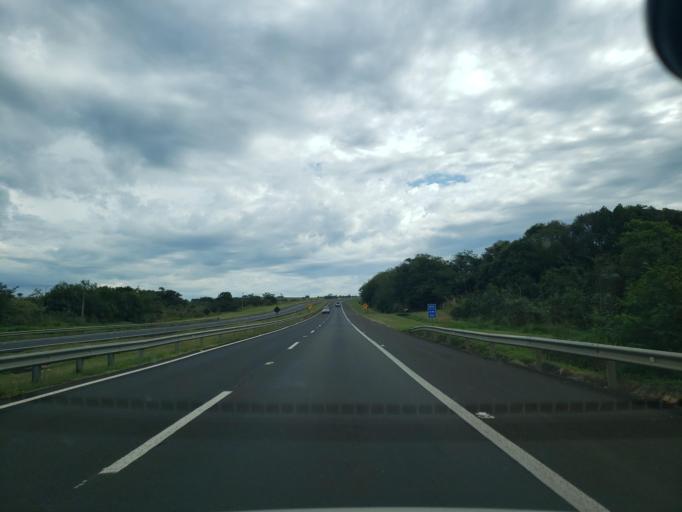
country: BR
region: Sao Paulo
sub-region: Bauru
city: Bauru
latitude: -22.1962
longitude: -49.1933
